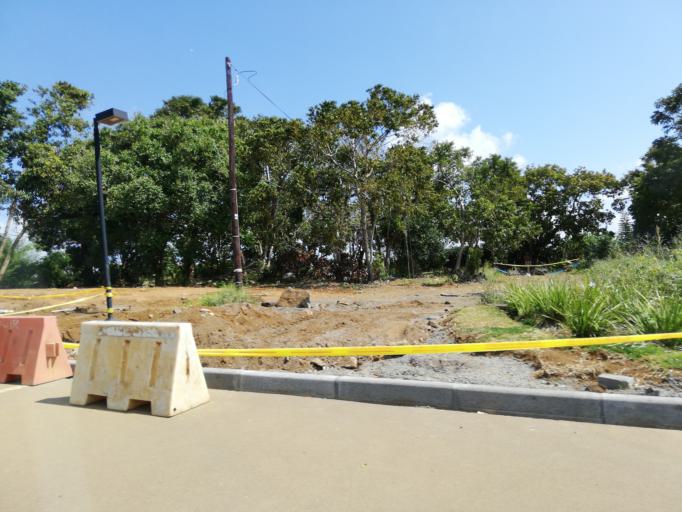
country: MU
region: Moka
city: Verdun
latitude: -20.2264
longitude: 57.5328
